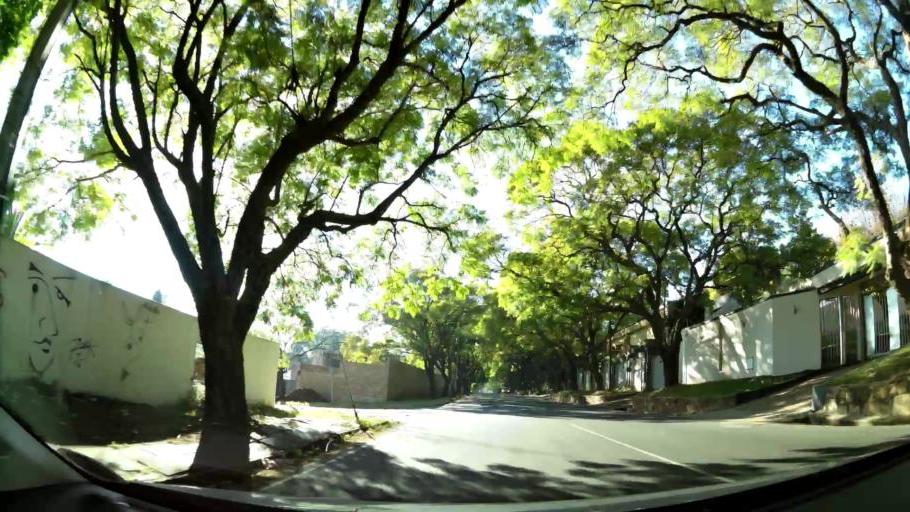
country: ZA
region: Gauteng
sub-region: City of Johannesburg Metropolitan Municipality
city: Johannesburg
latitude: -26.1699
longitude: 28.0683
